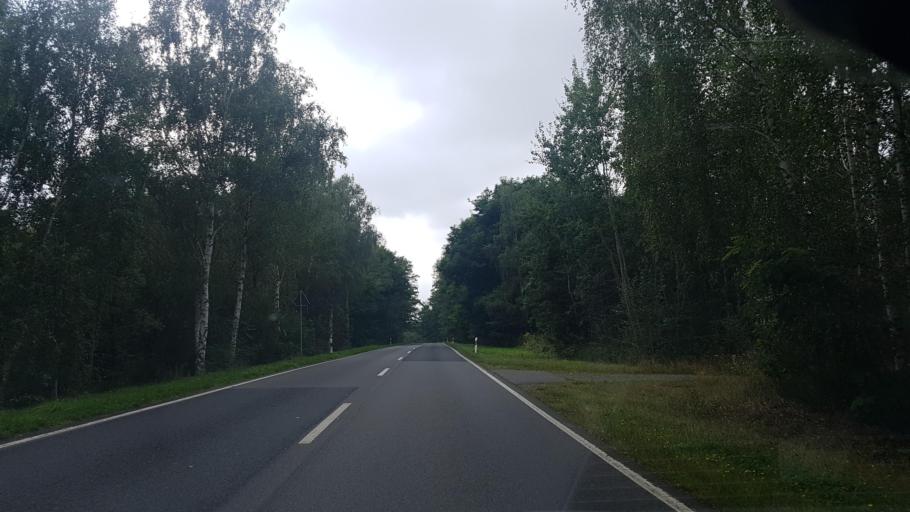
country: DE
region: Brandenburg
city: Lauchhammer
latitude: 51.5214
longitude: 13.7103
